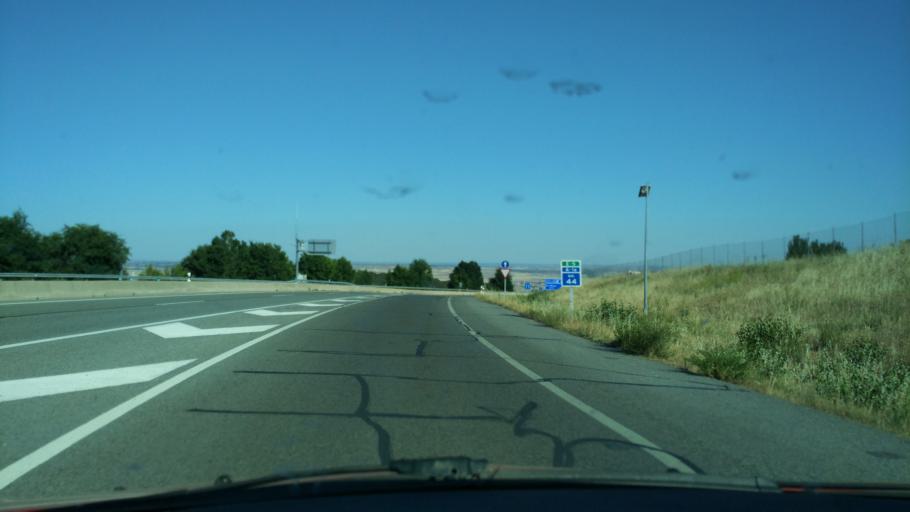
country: ES
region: Madrid
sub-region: Provincia de Madrid
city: Pedrezuela
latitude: 40.7438
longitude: -3.5910
